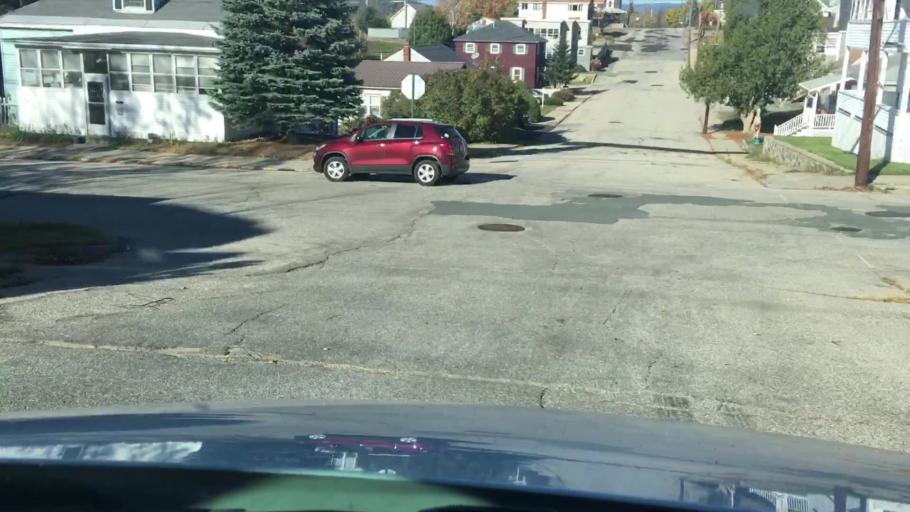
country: US
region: New Hampshire
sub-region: Coos County
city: Berlin
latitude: 44.4679
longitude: -71.1675
